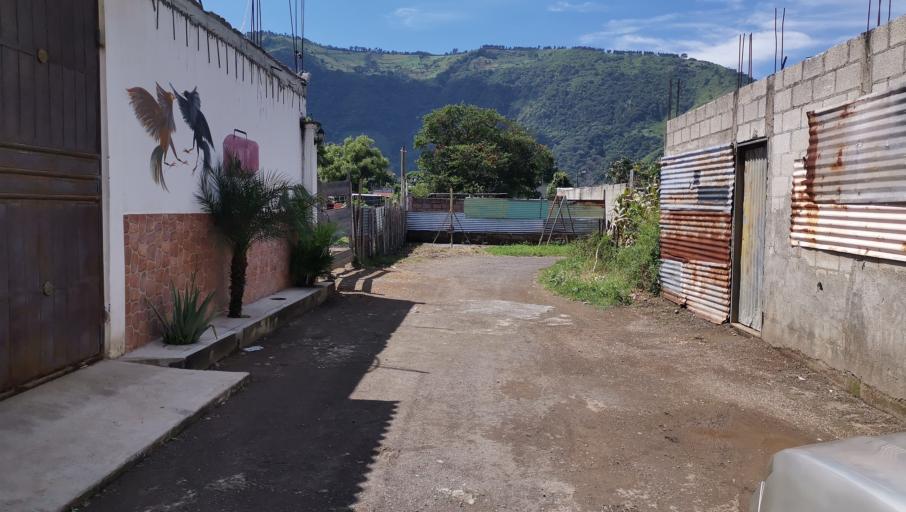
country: GT
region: Escuintla
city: San Vicente Pacaya
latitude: 14.4439
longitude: -90.6327
